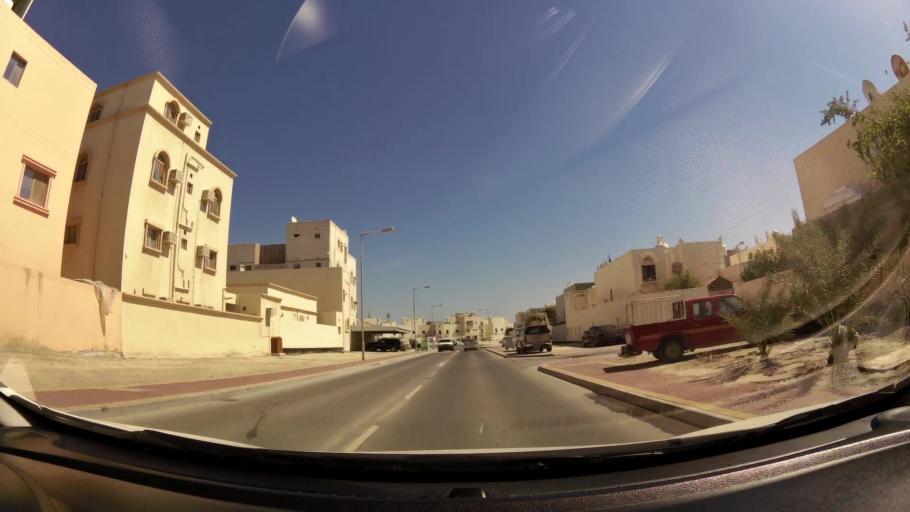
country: BH
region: Muharraq
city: Al Hadd
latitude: 26.2733
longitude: 50.6557
